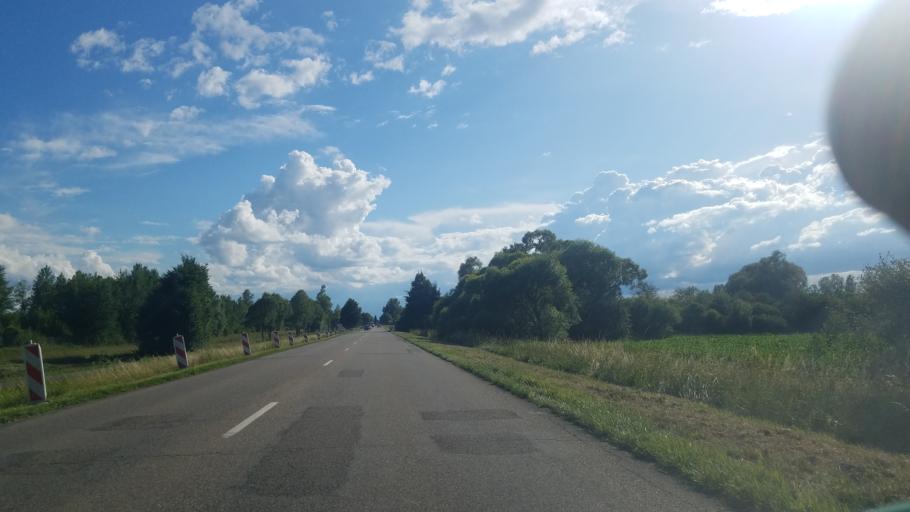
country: FR
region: Alsace
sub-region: Departement du Bas-Rhin
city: Drusenheim
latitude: 48.7485
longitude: 7.9326
